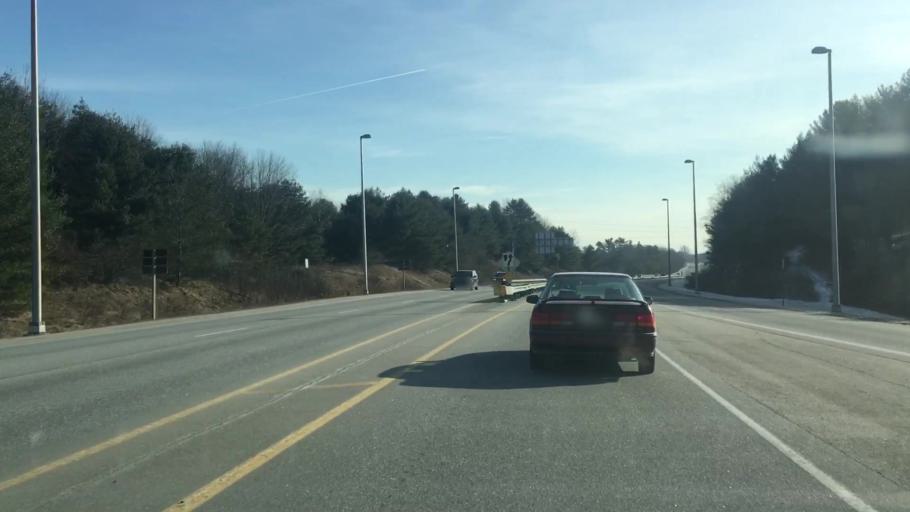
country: US
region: Maine
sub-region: Androscoggin County
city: Lewiston
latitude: 44.1192
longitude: -70.2209
